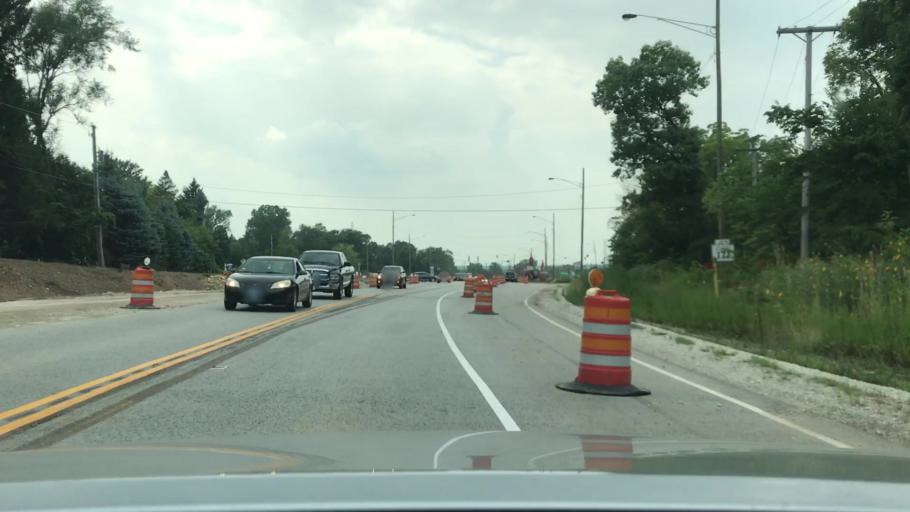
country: US
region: Illinois
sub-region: Will County
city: Goodings Grove
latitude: 41.6872
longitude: -87.9273
